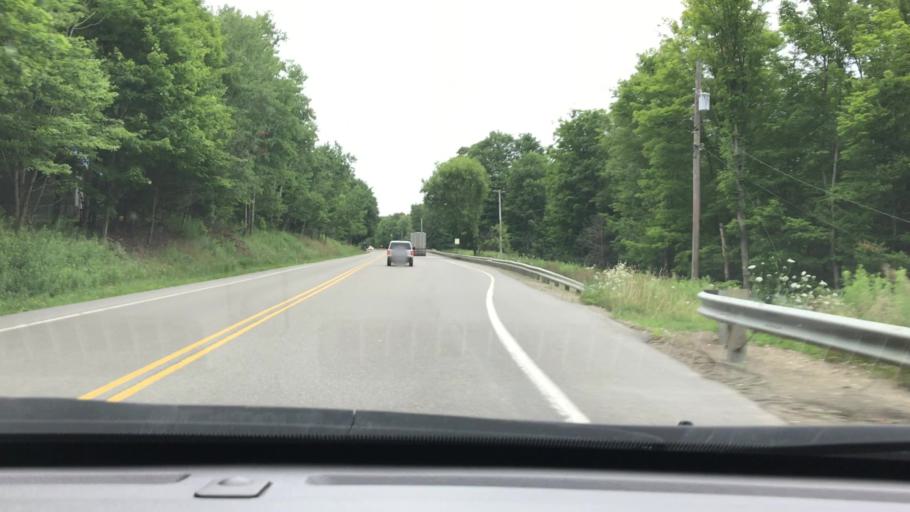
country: US
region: Pennsylvania
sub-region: McKean County
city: Kane
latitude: 41.6982
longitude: -78.6914
